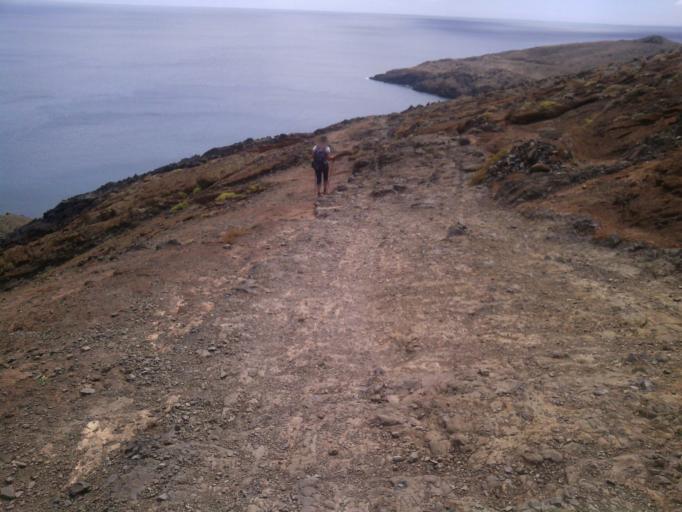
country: PT
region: Madeira
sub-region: Machico
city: Canical
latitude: 32.7500
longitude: -16.6957
